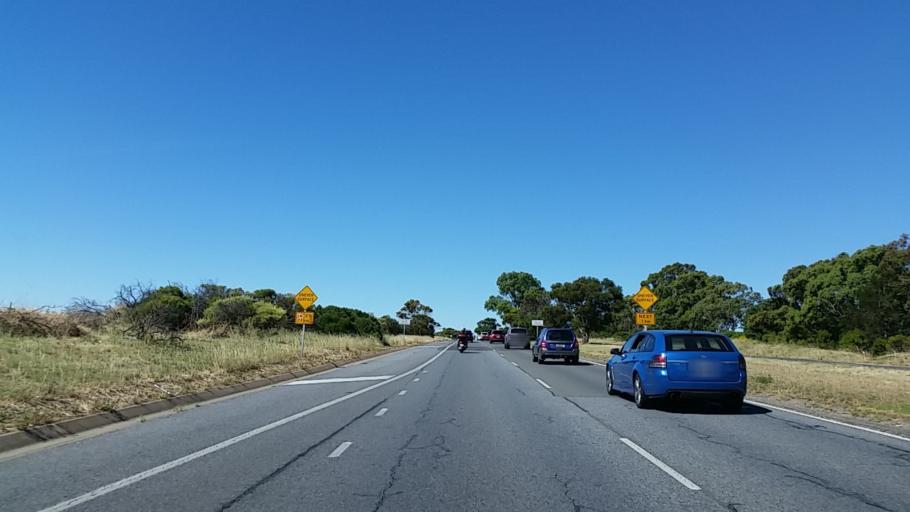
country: AU
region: South Australia
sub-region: Marion
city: Trott Park
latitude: -35.0690
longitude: 138.5285
